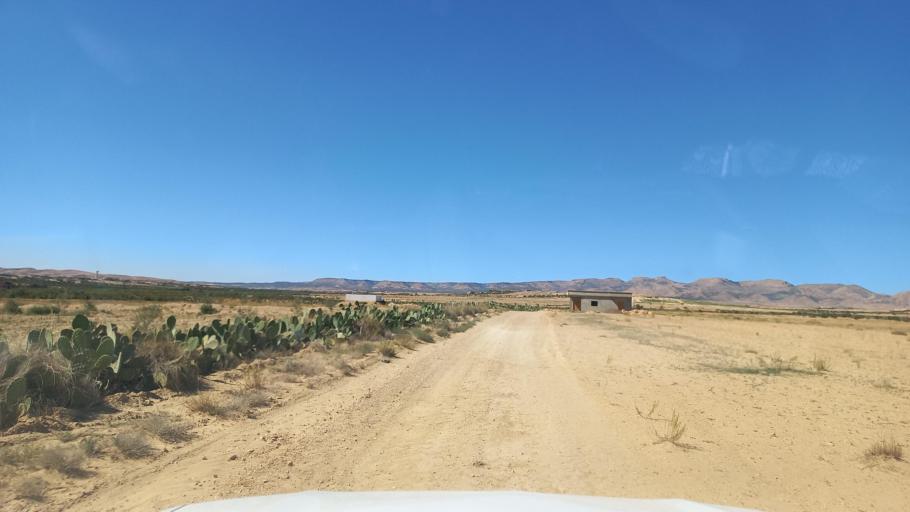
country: TN
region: Al Qasrayn
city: Sbiba
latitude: 35.3681
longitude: 9.0862
